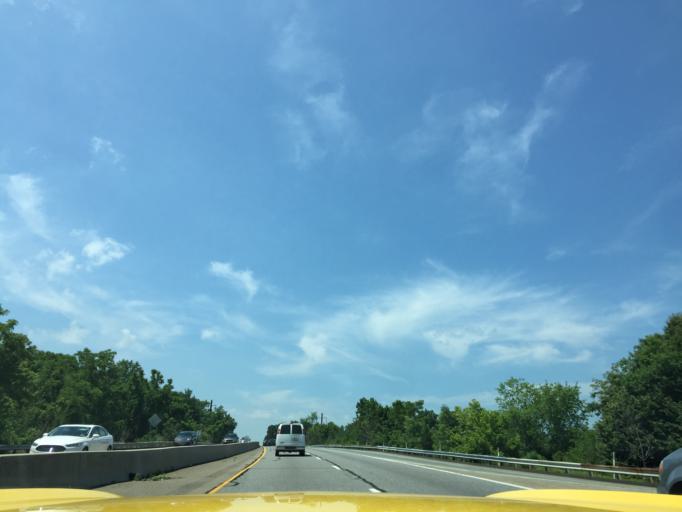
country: US
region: Pennsylvania
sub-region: Bucks County
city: Woodbourne
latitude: 40.1926
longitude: -74.8825
